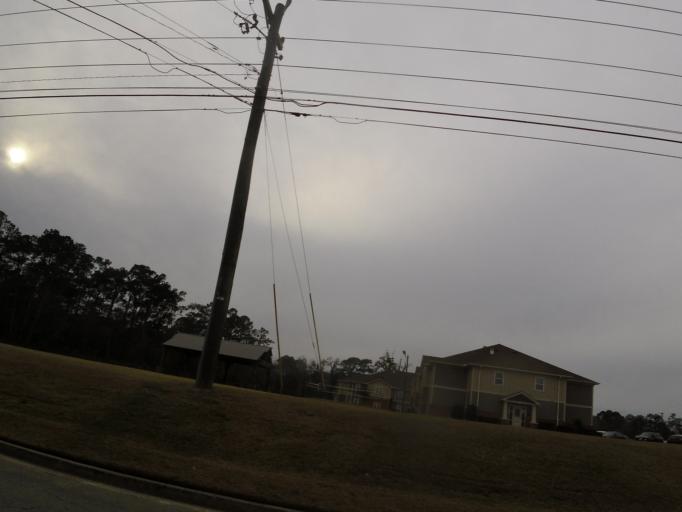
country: US
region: Georgia
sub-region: Thomas County
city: Thomasville
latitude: 30.8125
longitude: -83.9803
